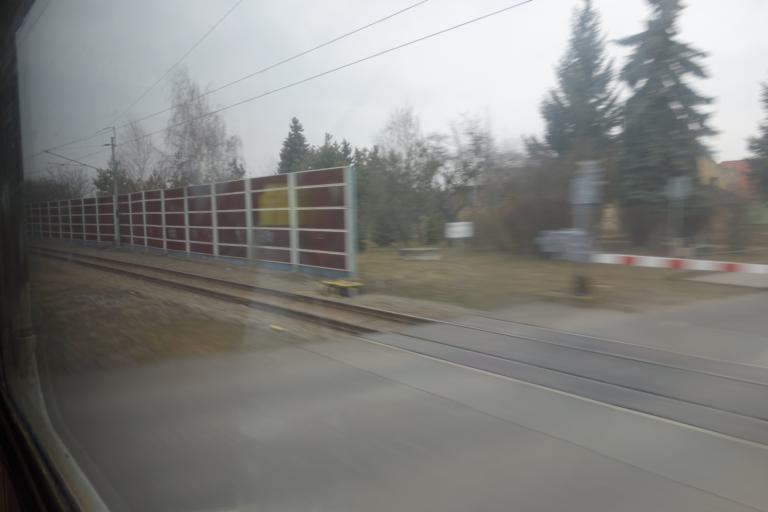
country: CZ
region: Central Bohemia
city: Horni Pocaply
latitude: 50.4225
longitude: 14.3870
